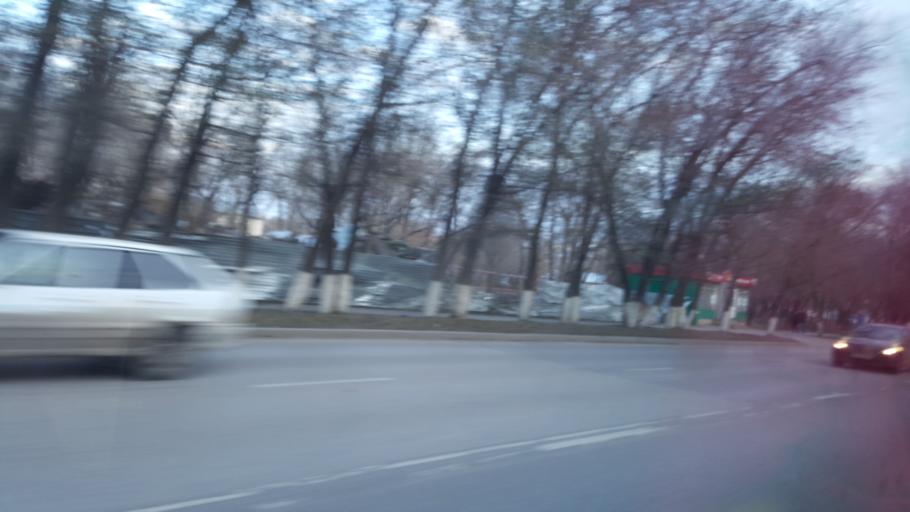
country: KZ
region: Astana Qalasy
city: Astana
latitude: 51.1669
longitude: 71.4503
